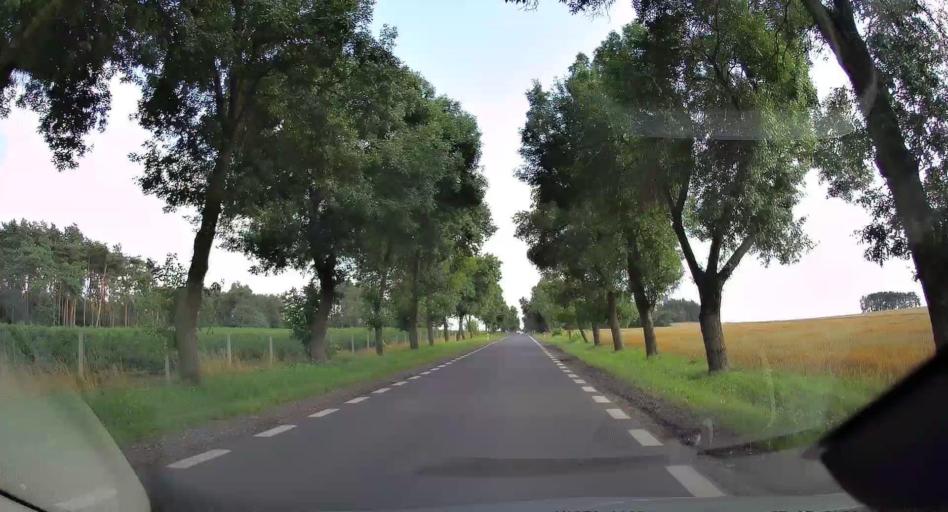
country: PL
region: Lodz Voivodeship
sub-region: Powiat tomaszowski
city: Rzeczyca
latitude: 51.6386
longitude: 20.2884
